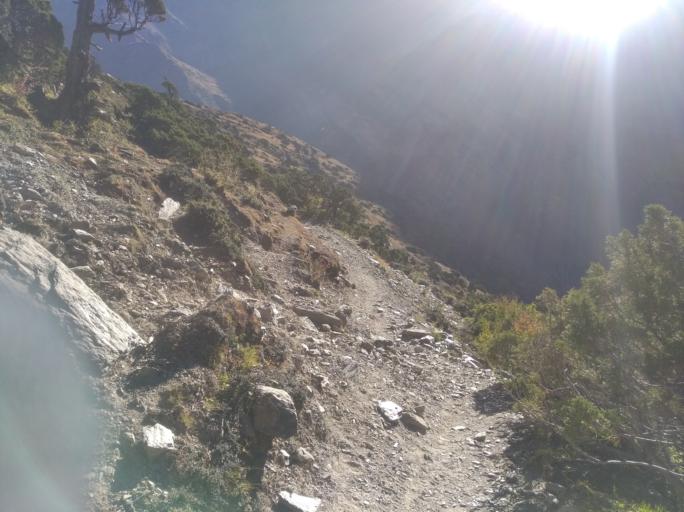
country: NP
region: Western Region
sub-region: Dhawalagiri Zone
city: Jomsom
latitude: 28.8983
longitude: 83.3596
